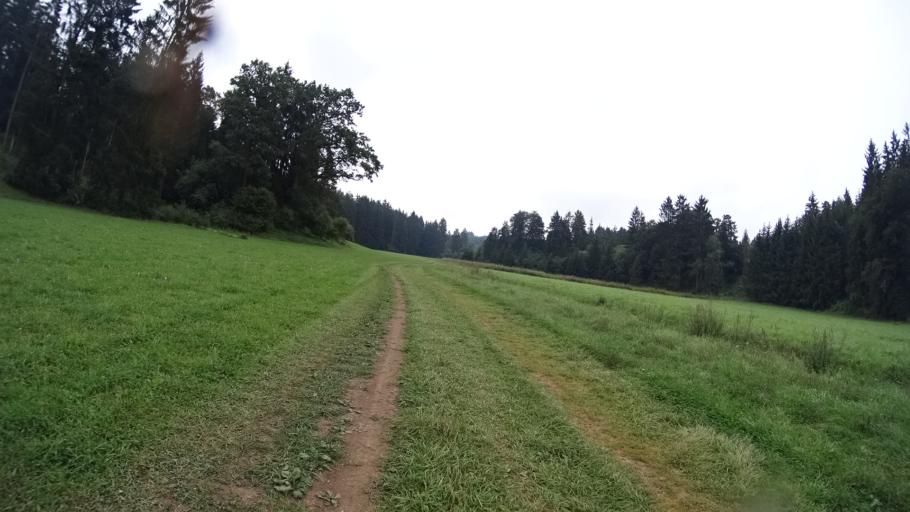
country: DE
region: Bavaria
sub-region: Upper Bavaria
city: Bohmfeld
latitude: 48.8832
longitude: 11.3525
